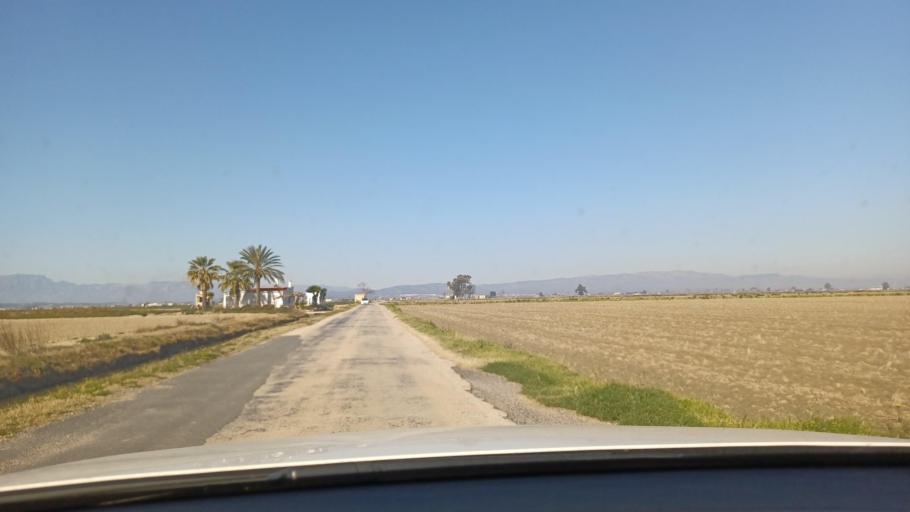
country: ES
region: Catalonia
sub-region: Provincia de Tarragona
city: Deltebre
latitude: 40.6828
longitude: 0.6567
